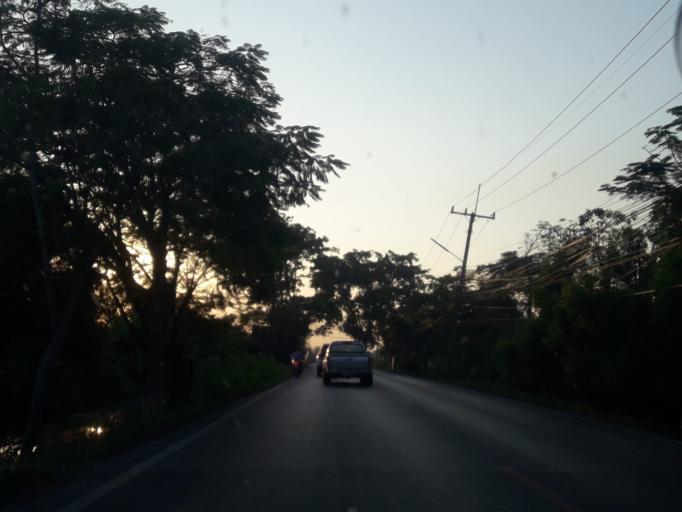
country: TH
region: Pathum Thani
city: Nong Suea
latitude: 14.1316
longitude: 100.8021
